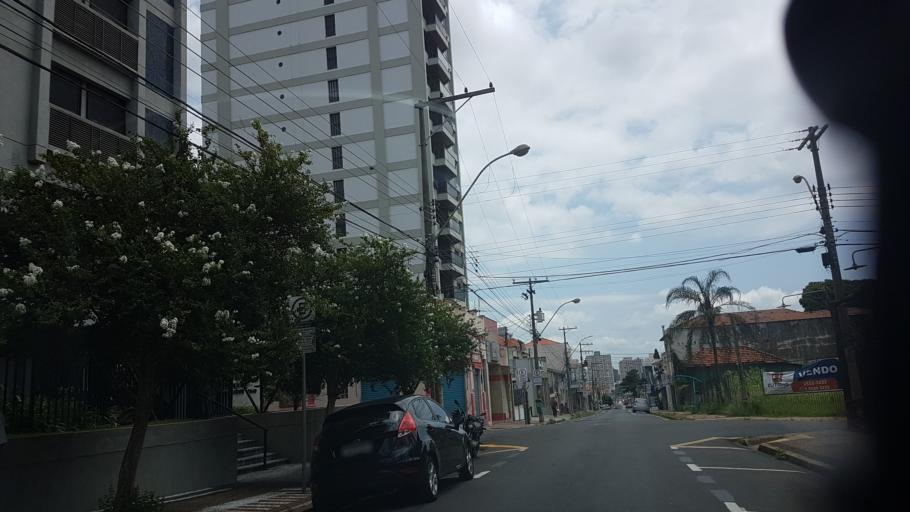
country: BR
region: Sao Paulo
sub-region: Piracicaba
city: Piracicaba
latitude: -22.7348
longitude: -47.6523
